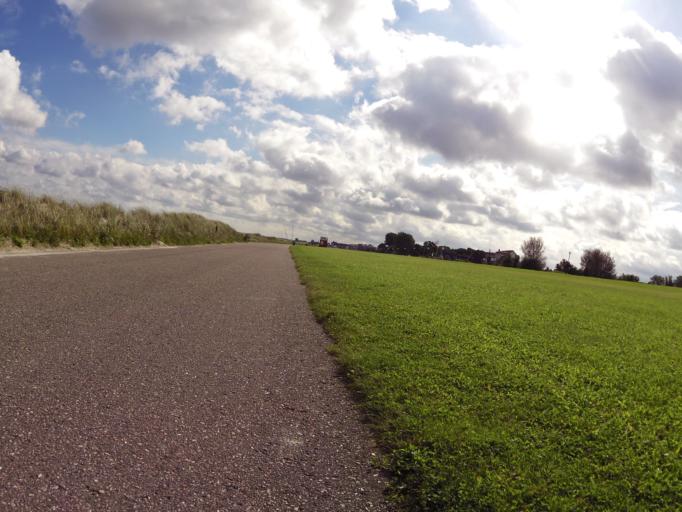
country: DE
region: Schleswig-Holstein
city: Krummbek
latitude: 54.4197
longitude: 10.4044
